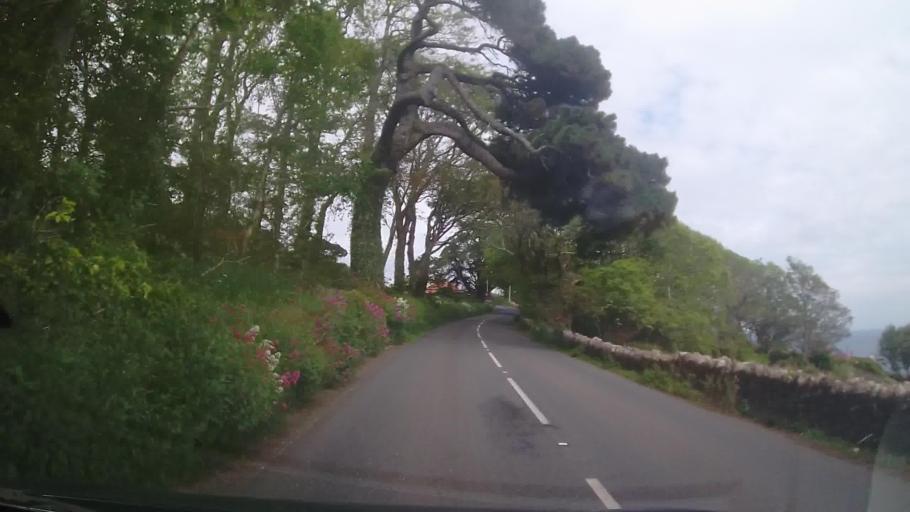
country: GB
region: England
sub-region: Devon
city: Dartmouth
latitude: 50.3202
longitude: -3.6014
